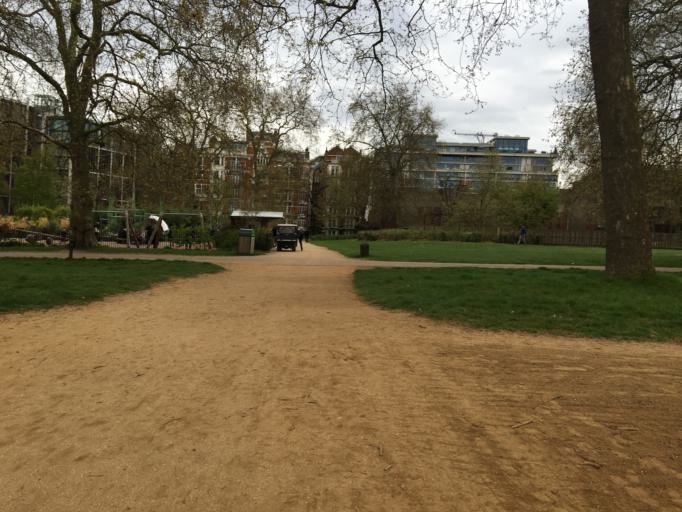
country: GB
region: England
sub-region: Greater London
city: Chelsea
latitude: 51.5036
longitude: -0.1631
